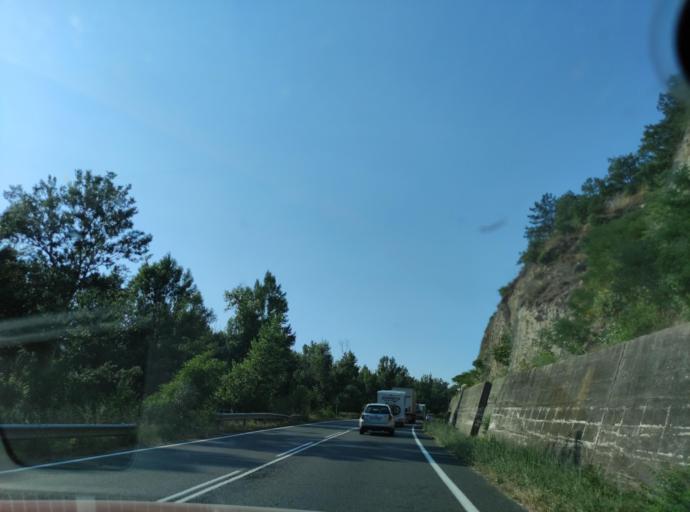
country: BG
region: Blagoevgrad
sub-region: Obshtina Simitli
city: Simitli
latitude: 41.8752
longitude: 23.1215
